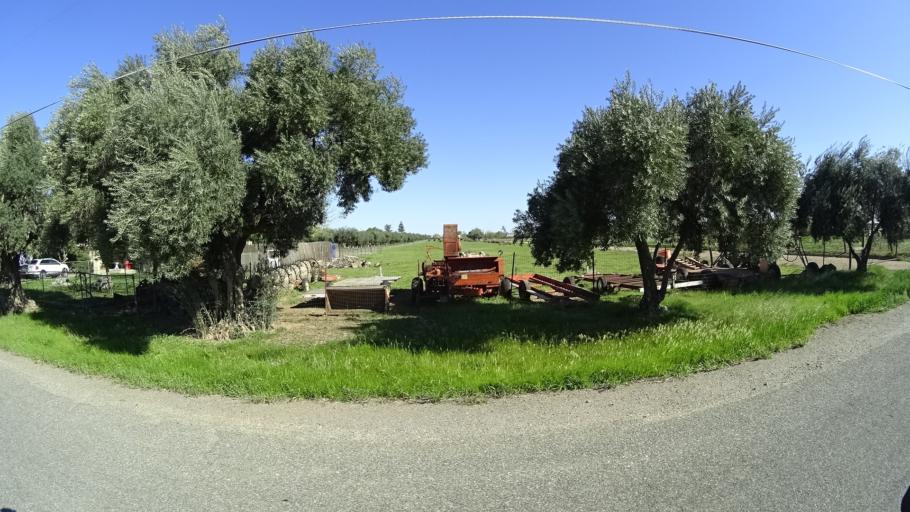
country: US
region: California
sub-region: Glenn County
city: Orland
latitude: 39.7369
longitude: -122.2301
